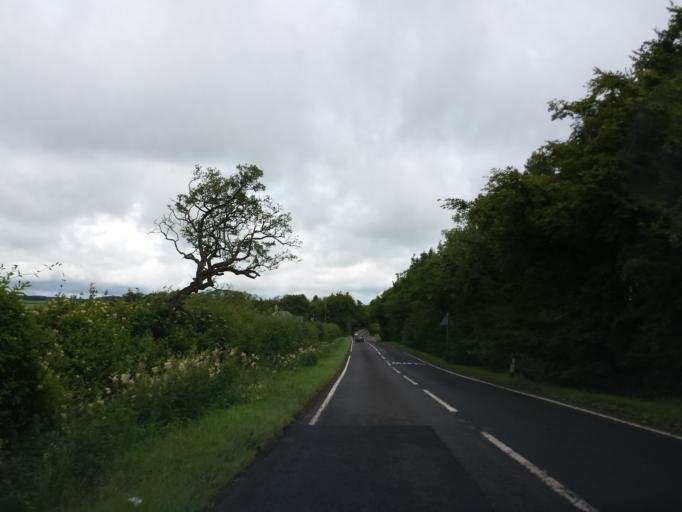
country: GB
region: Scotland
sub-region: Fife
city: Strathkinness
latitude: 56.2893
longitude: -2.8296
